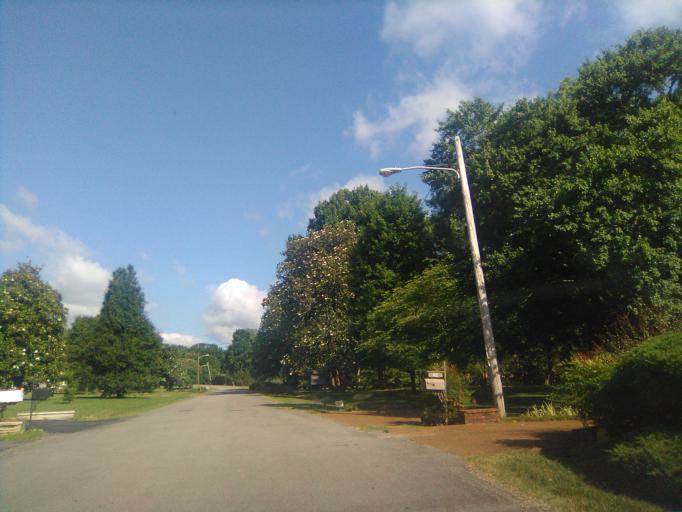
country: US
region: Tennessee
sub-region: Davidson County
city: Belle Meade
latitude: 36.1135
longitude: -86.8651
